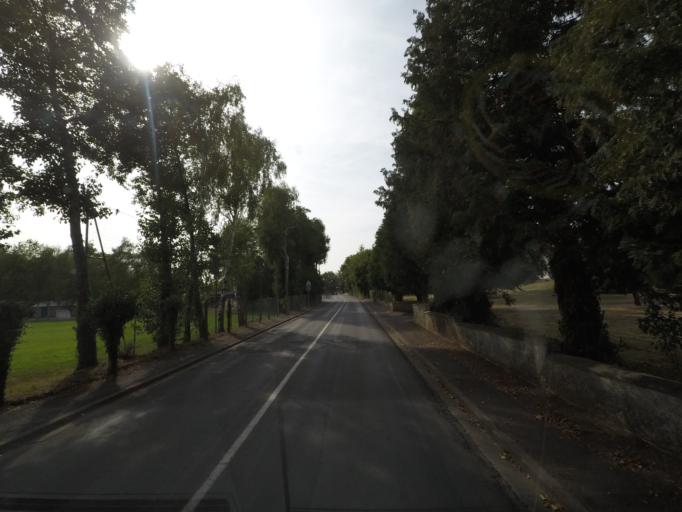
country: FR
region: Poitou-Charentes
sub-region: Departement des Deux-Sevres
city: Melle
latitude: 46.2302
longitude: -0.1329
